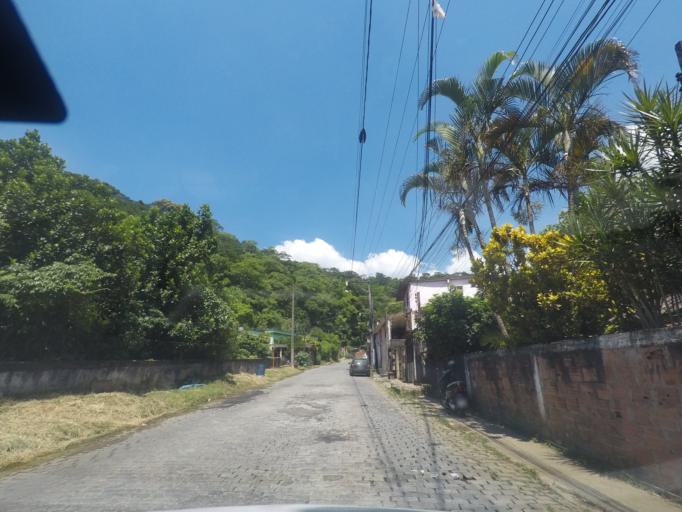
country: BR
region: Rio de Janeiro
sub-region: Petropolis
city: Petropolis
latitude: -22.5699
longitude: -43.1853
